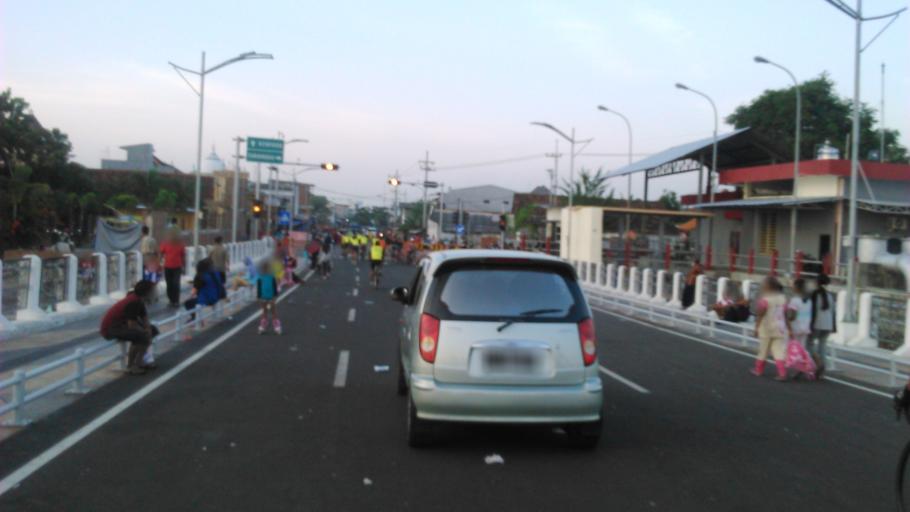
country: ID
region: East Java
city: Labansari
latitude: -7.2402
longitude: 112.7976
